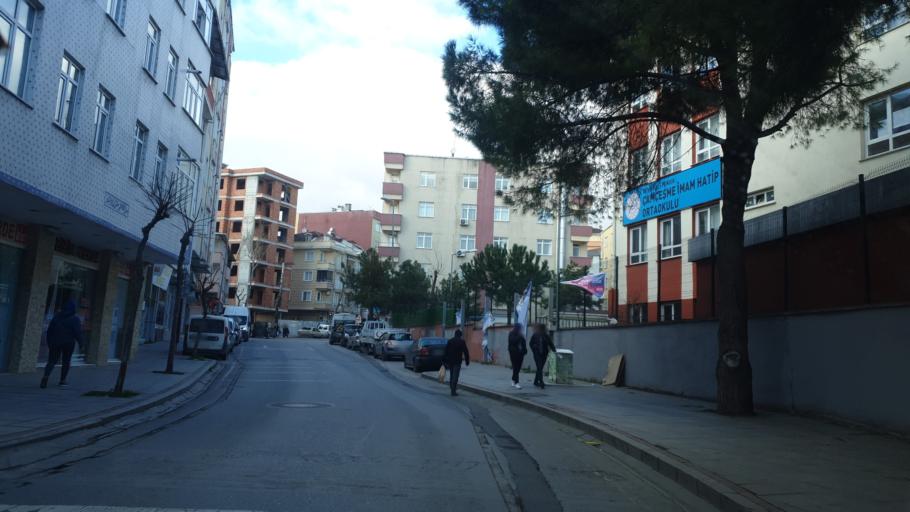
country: TR
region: Istanbul
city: Pendik
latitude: 40.8742
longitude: 29.2727
